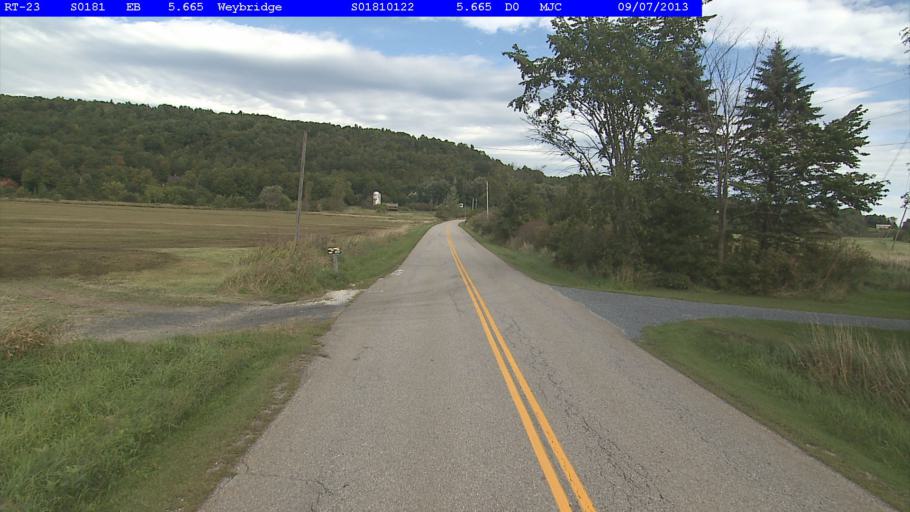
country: US
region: Vermont
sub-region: Addison County
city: Vergennes
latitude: 44.0723
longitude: -73.2520
